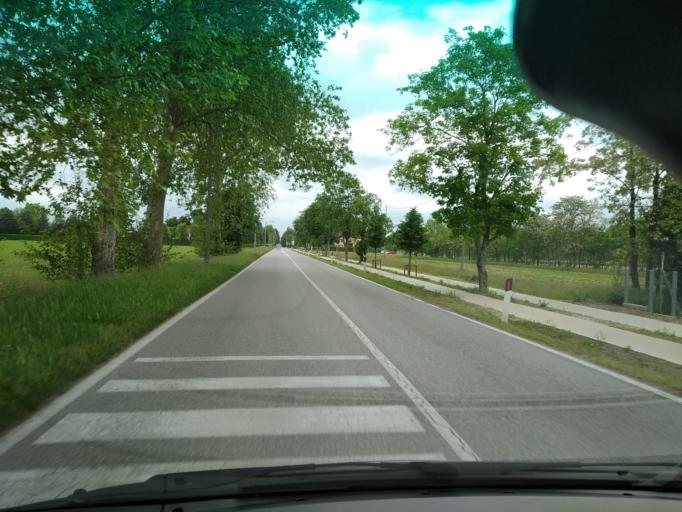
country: IT
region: Veneto
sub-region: Provincia di Padova
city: Piazzola sul Brenta
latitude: 45.5320
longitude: 11.7914
